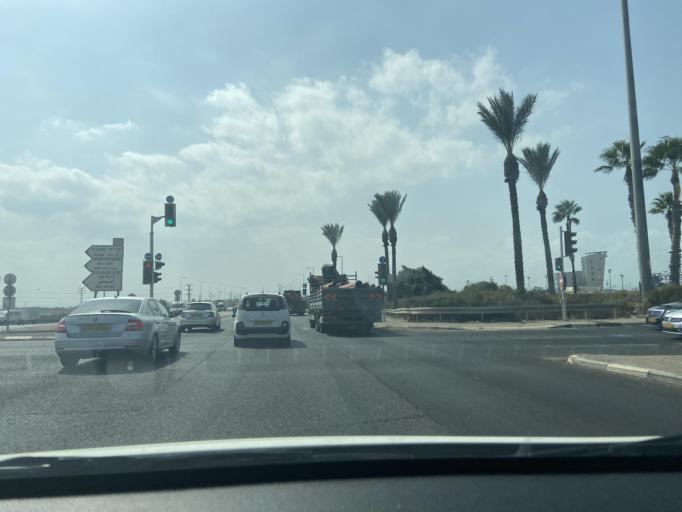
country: IL
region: Northern District
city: `Akko
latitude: 32.9192
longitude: 35.0968
